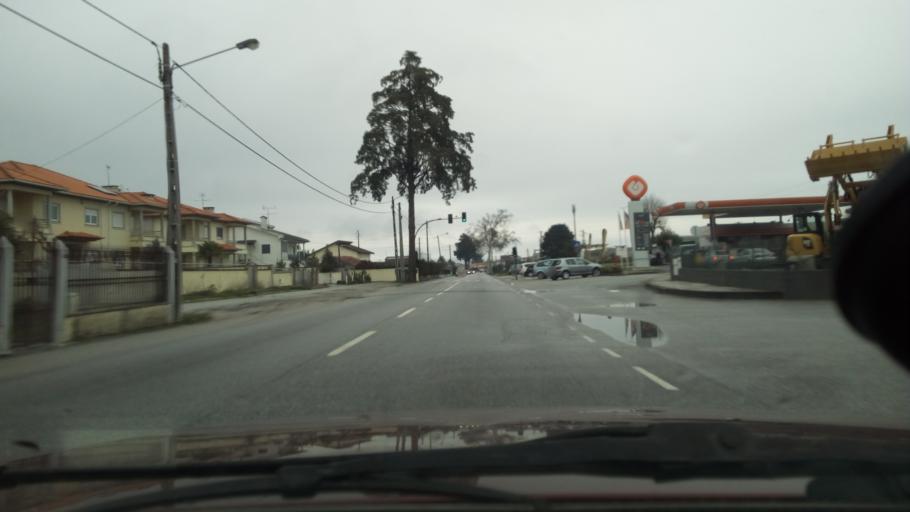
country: PT
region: Viseu
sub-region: Viseu
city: Rio de Loba
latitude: 40.6431
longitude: -7.8640
